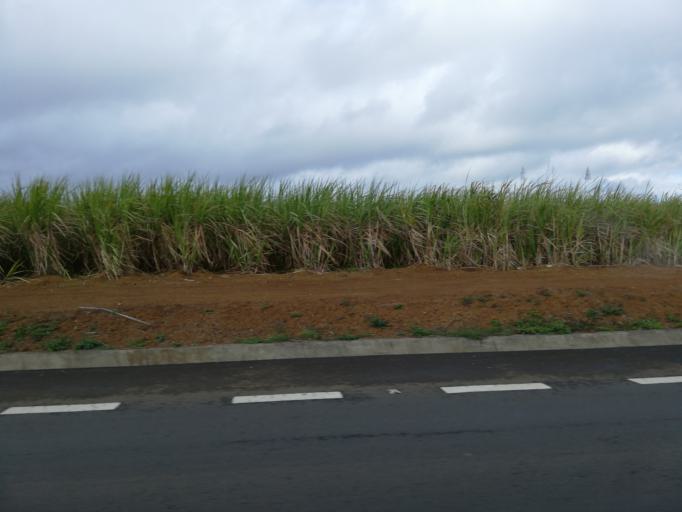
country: MU
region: Moka
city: Verdun
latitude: -20.2308
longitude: 57.5341
